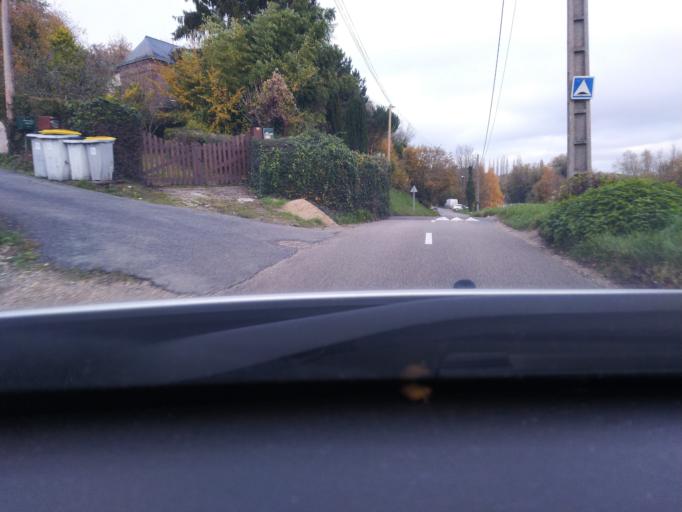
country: FR
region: Haute-Normandie
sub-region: Departement de la Seine-Maritime
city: Duclair
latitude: 49.4803
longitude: 0.8692
